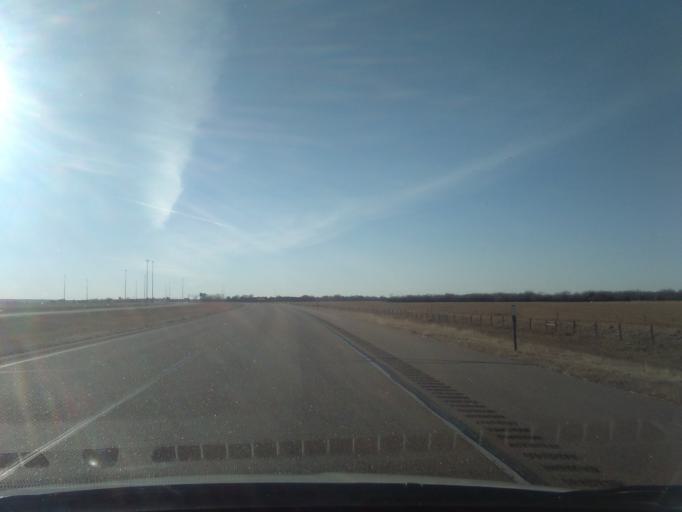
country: US
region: Colorado
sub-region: Sedgwick County
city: Julesburg
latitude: 41.0355
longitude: -102.1384
